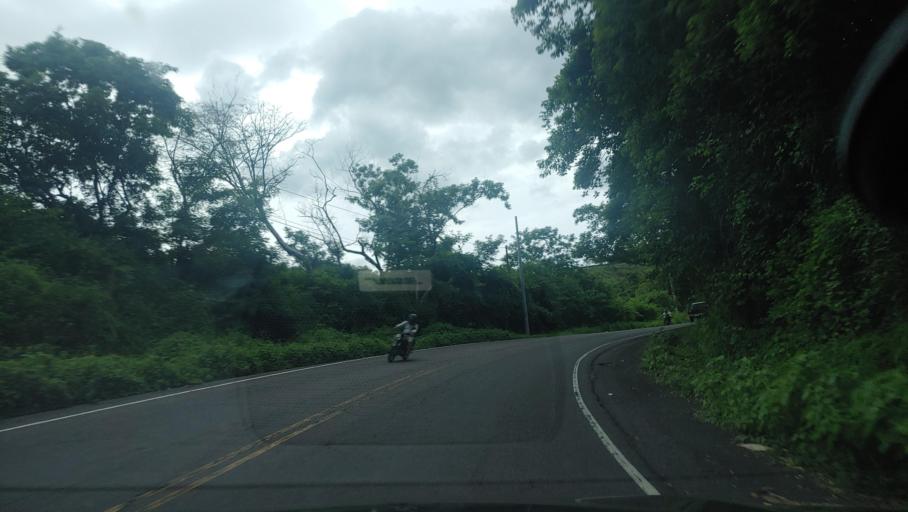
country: HN
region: Choluteca
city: Santa Ana de Yusguare
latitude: 13.3730
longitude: -87.0676
